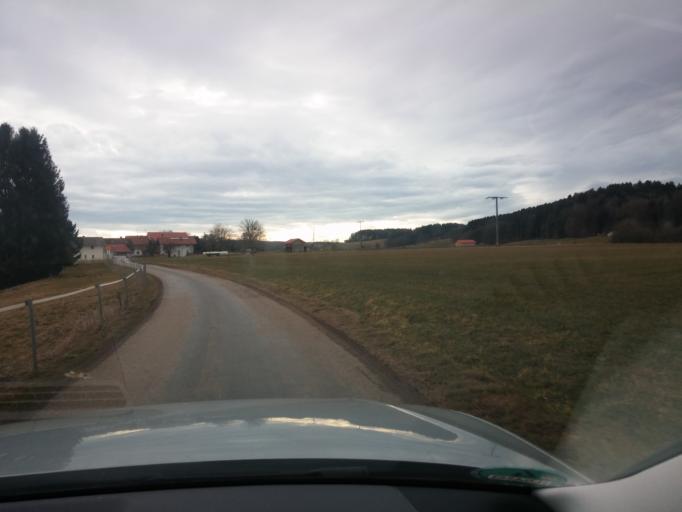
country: DE
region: Bavaria
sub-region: Upper Bavaria
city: Glonn
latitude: 48.0041
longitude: 11.8681
